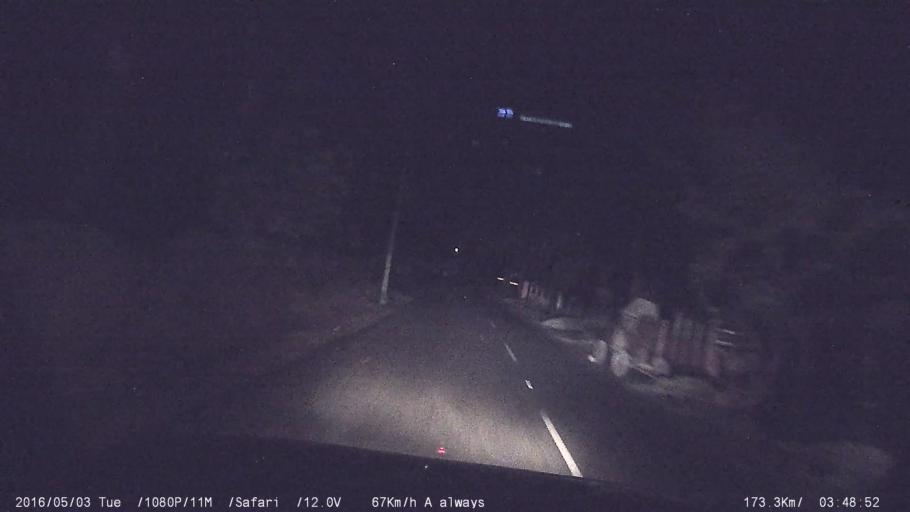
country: IN
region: Kerala
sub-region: Kottayam
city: Palackattumala
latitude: 9.8150
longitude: 76.6117
